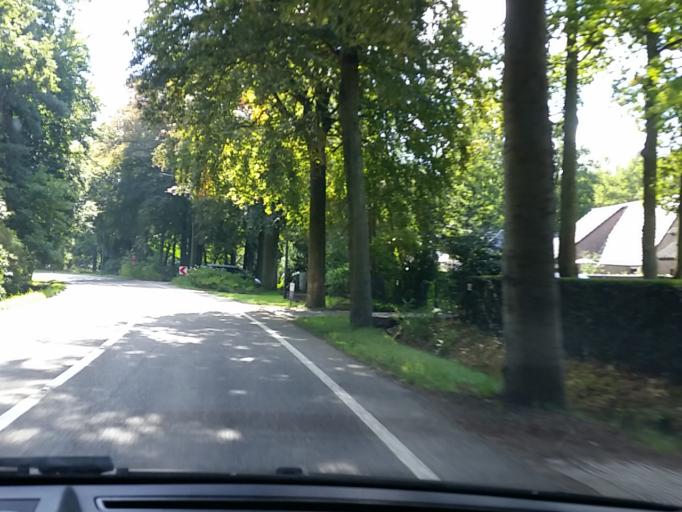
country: BE
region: Flanders
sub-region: Provincie Antwerpen
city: Schilde
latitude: 51.2544
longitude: 4.5605
